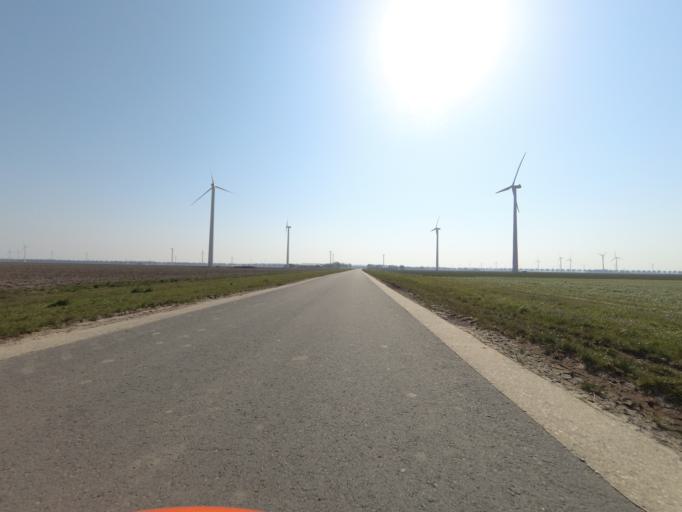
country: NL
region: Utrecht
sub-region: Gemeente Bunschoten
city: Spakenburg
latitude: 52.3360
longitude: 5.3848
